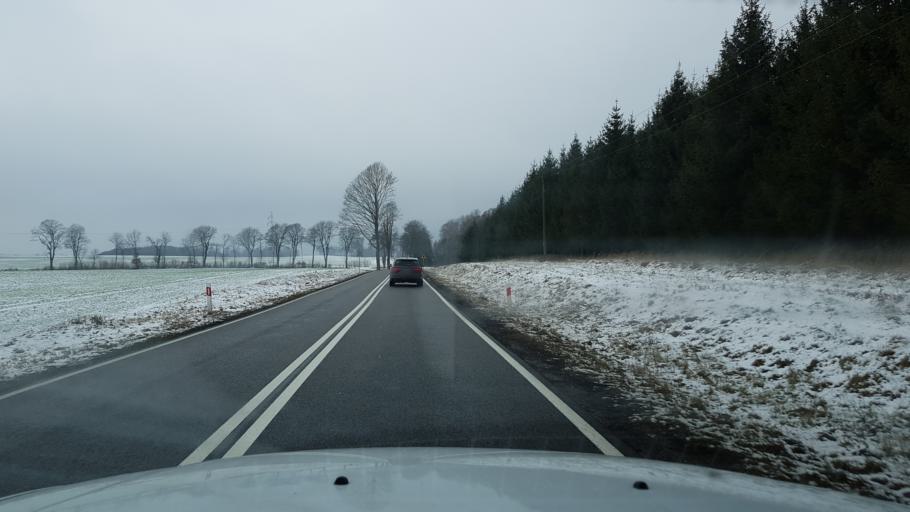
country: PL
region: West Pomeranian Voivodeship
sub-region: Powiat drawski
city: Zlocieniec
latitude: 53.5311
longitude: 16.0638
